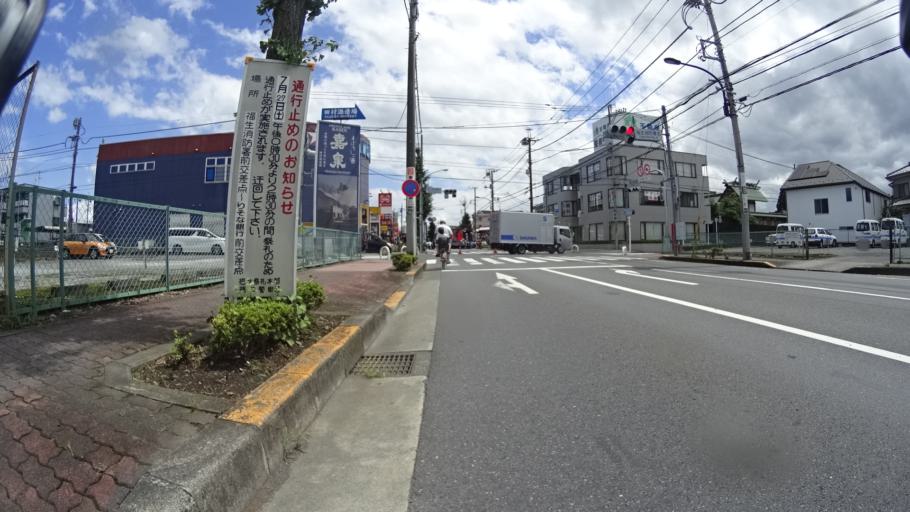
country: JP
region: Tokyo
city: Fussa
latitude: 35.7450
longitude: 139.3238
